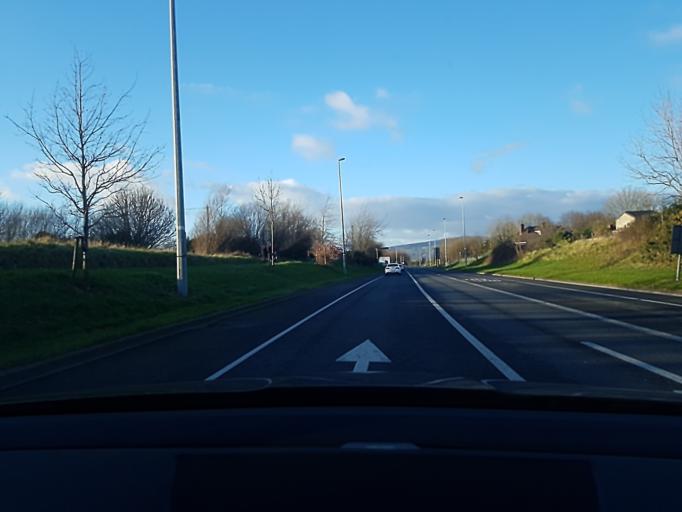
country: IE
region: Munster
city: Moyross
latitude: 52.6628
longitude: -8.6672
